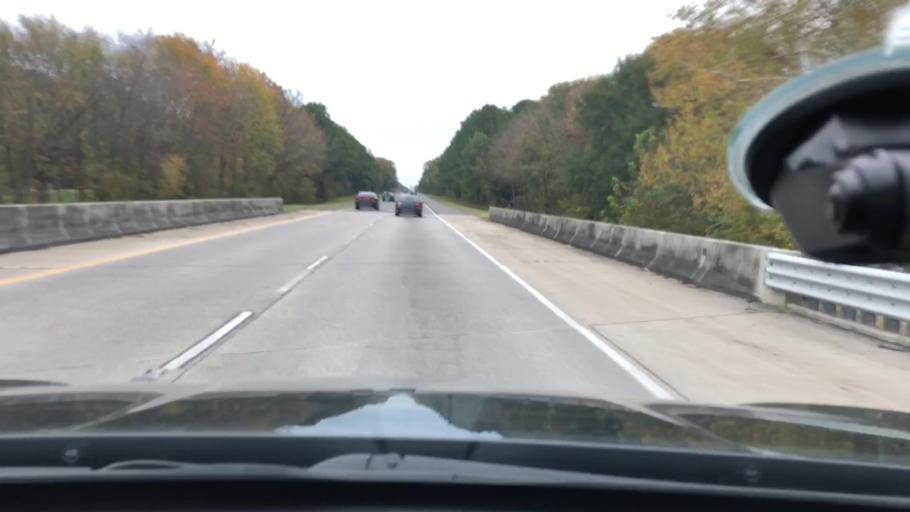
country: US
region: Arkansas
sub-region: Hempstead County
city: Hope
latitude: 33.6354
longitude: -93.7109
